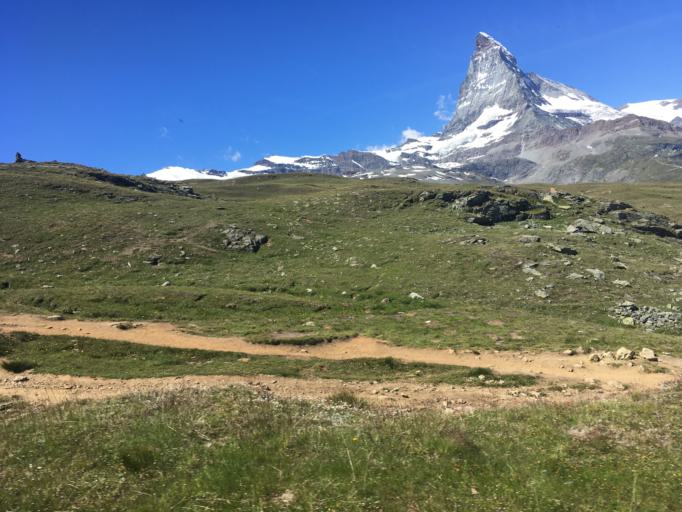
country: CH
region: Valais
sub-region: Visp District
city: Zermatt
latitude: 45.9911
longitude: 7.7554
